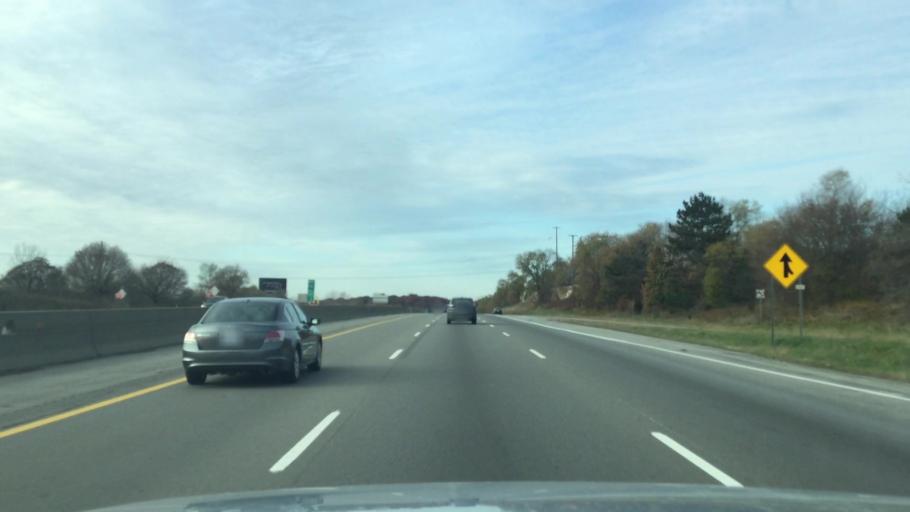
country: US
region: Michigan
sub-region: Washtenaw County
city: Ypsilanti
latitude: 42.2283
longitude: -83.6195
